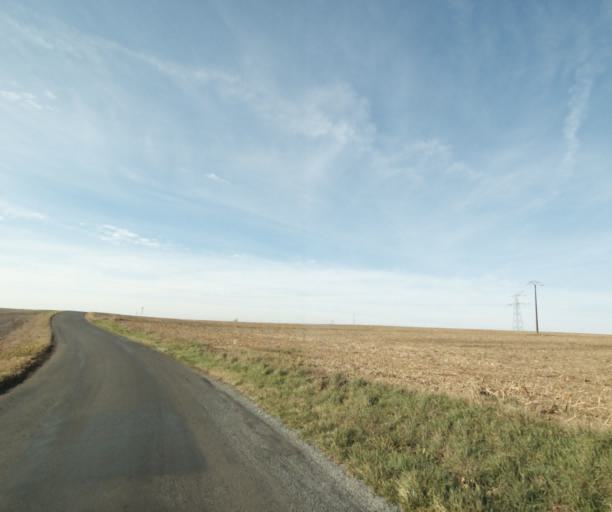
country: FR
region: Poitou-Charentes
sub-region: Departement de la Charente-Maritime
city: Les Gonds
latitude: 45.7328
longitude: -0.5901
